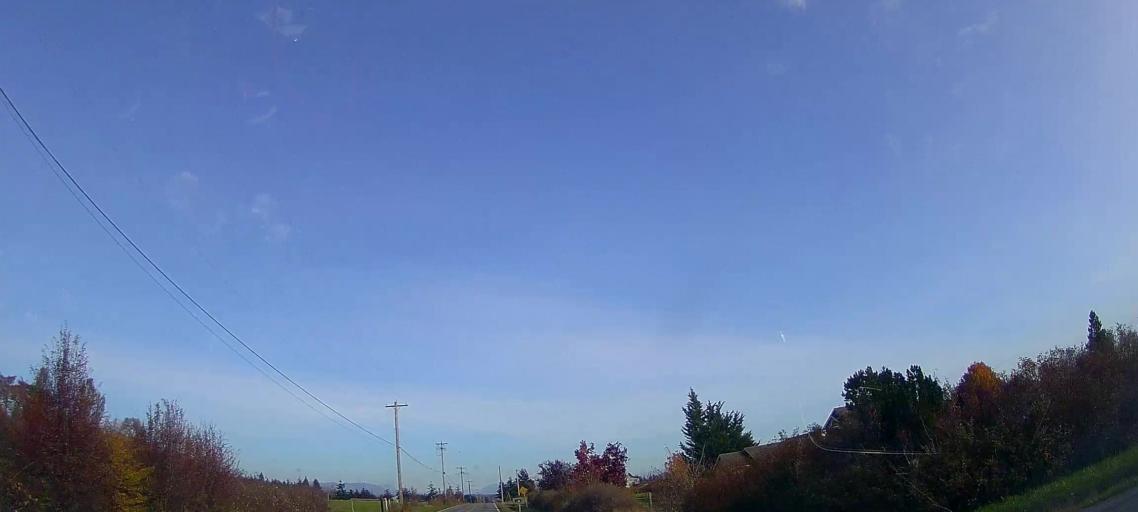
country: US
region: Washington
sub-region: Snohomish County
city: Stanwood
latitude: 48.2545
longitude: -122.4446
